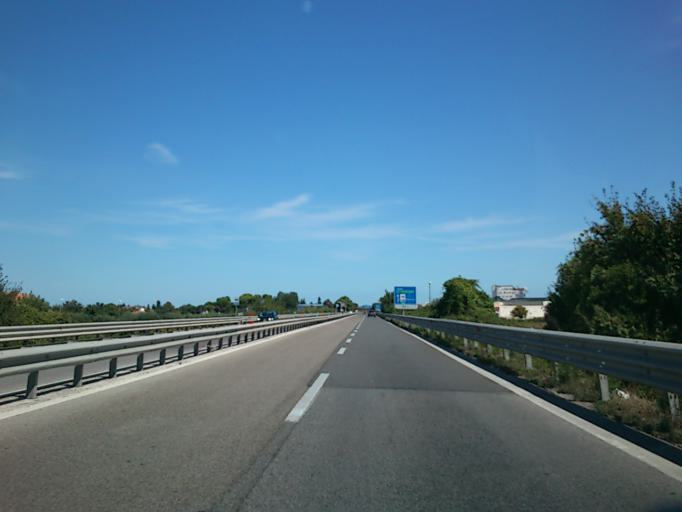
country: IT
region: The Marches
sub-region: Provincia di Pesaro e Urbino
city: Bellocchi
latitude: 43.7986
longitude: 13.0080
